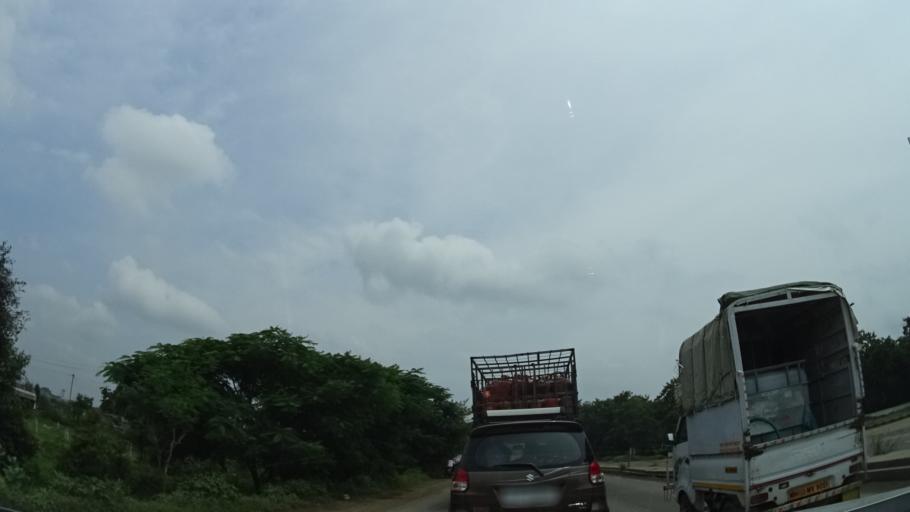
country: IN
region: Maharashtra
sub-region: Pune Division
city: Koregaon
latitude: 18.6584
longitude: 74.0848
